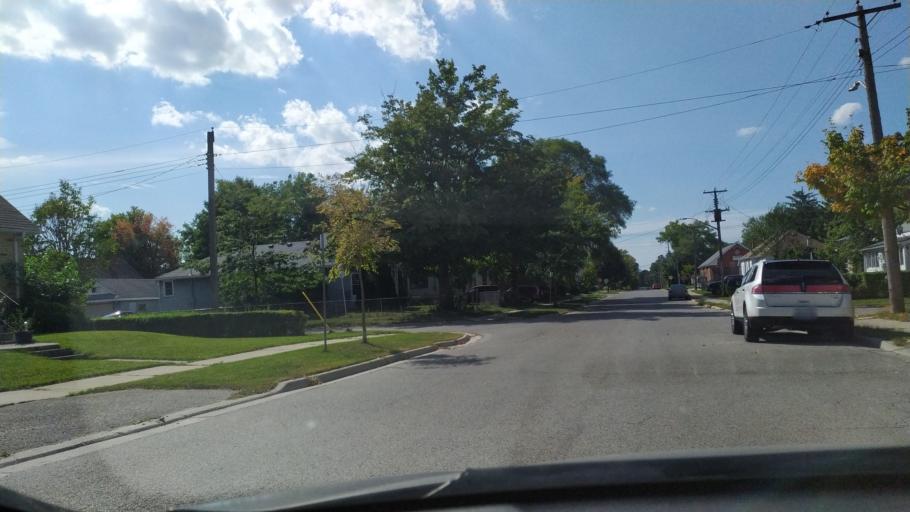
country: CA
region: Ontario
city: London
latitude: 42.9648
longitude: -81.2630
